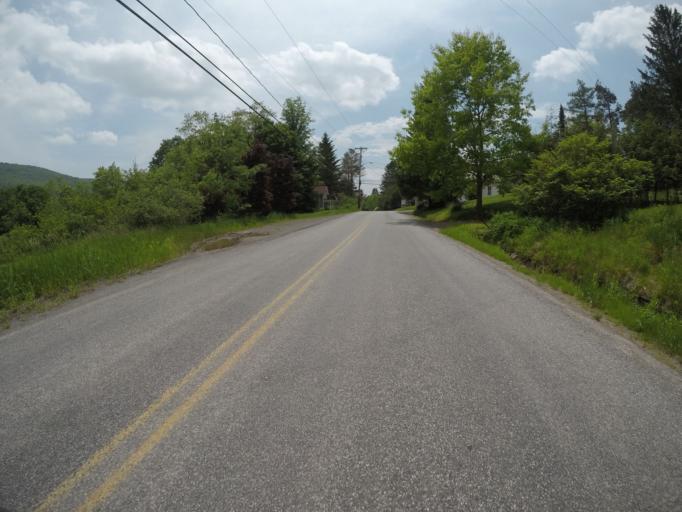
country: US
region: New York
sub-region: Delaware County
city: Stamford
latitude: 42.2143
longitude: -74.6819
